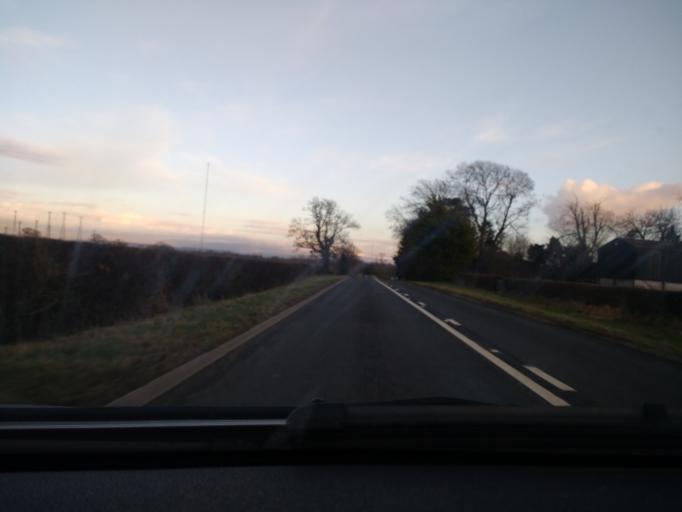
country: GB
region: England
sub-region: Cumbria
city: Scotby
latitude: 54.7295
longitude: -2.9167
